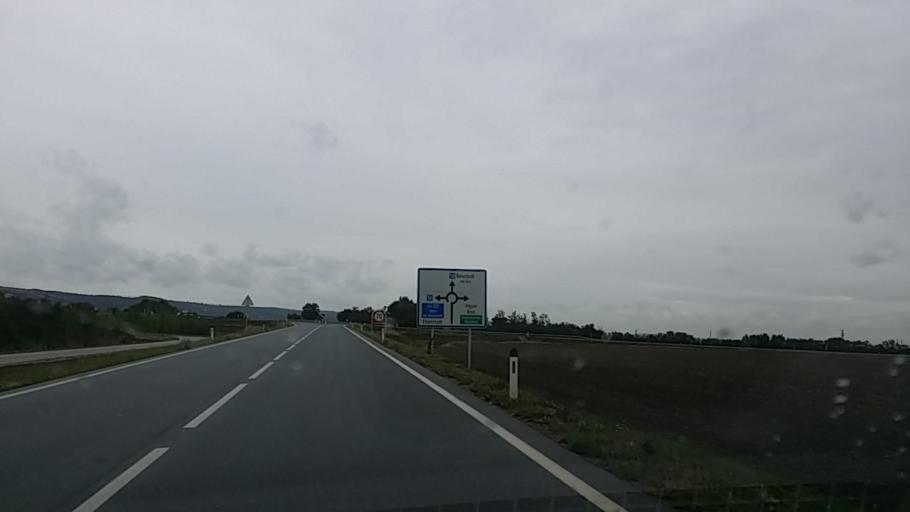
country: AT
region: Burgenland
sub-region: Eisenstadt-Umgebung
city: Schutzen am Gebirge
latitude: 47.8666
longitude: 16.6466
